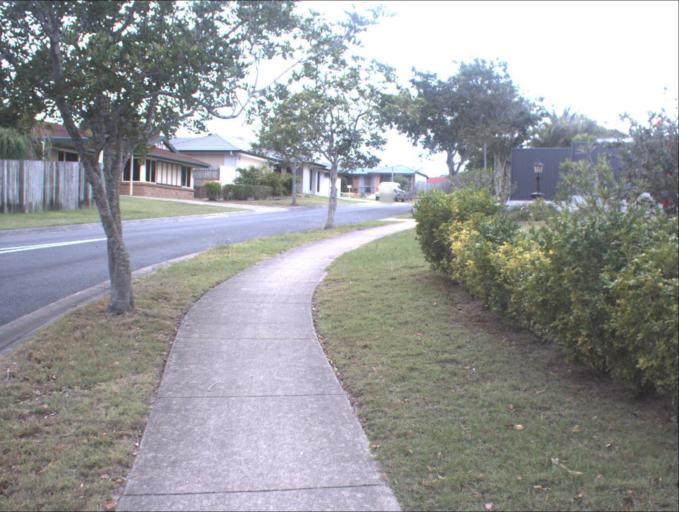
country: AU
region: Queensland
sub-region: Logan
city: Park Ridge South
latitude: -27.6769
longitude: 153.0444
